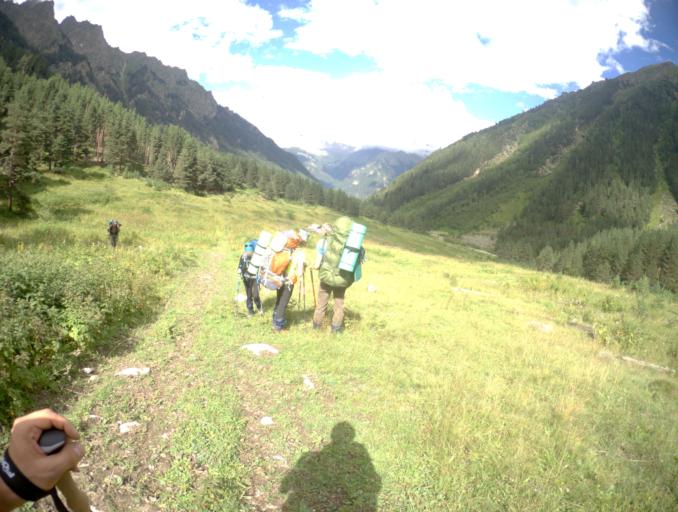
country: RU
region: Karachayevo-Cherkesiya
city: Uchkulan
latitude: 43.3460
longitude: 42.1516
